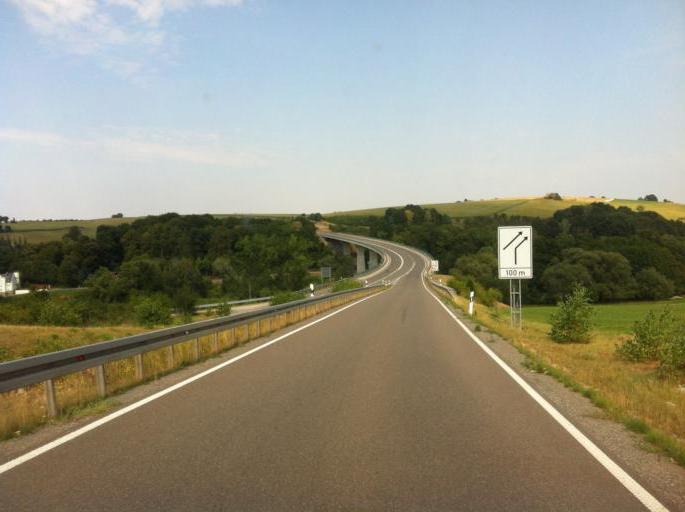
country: DE
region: Saxony
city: Reichenbach/Vogtland
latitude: 50.6096
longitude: 12.3167
